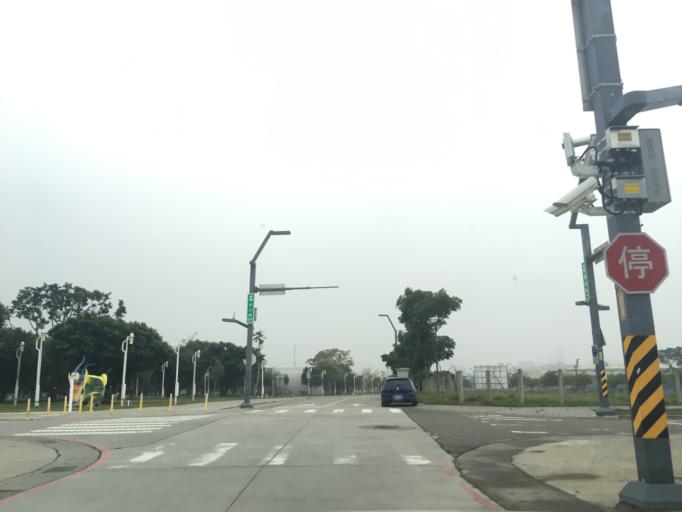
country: TW
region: Taiwan
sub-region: Taichung City
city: Taichung
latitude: 24.1914
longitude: 120.6520
